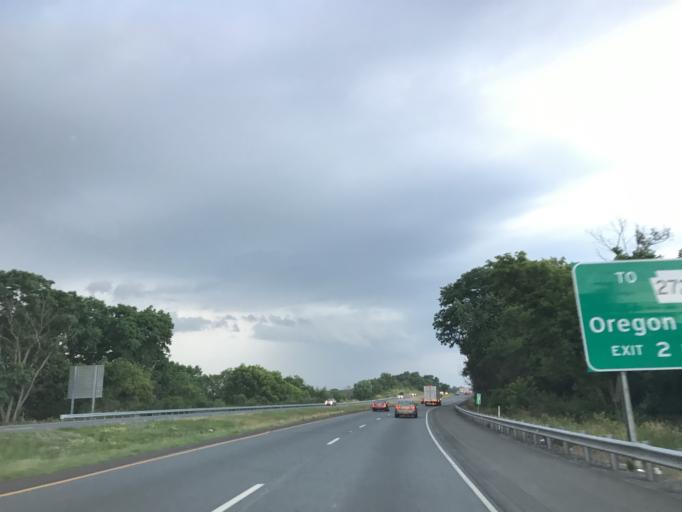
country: US
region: Pennsylvania
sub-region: Lancaster County
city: Lancaster
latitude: 40.0762
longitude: -76.2843
